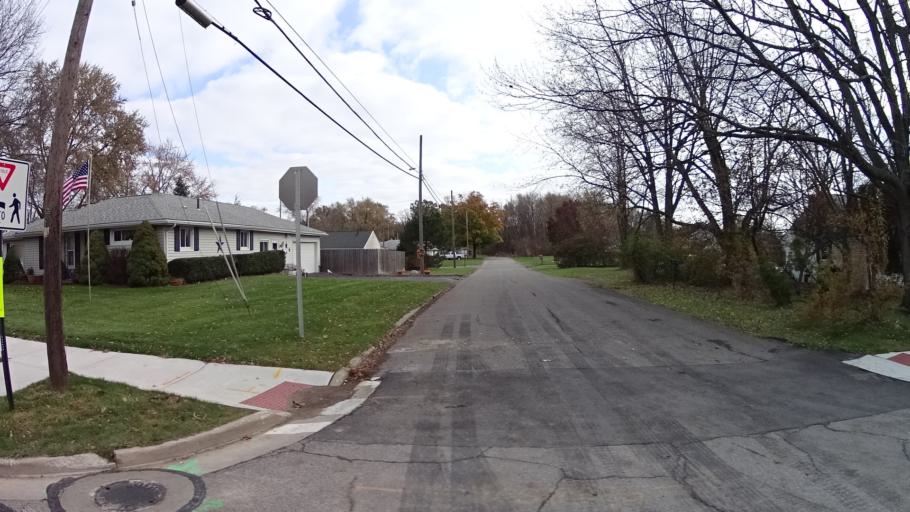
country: US
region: Ohio
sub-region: Lorain County
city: Sheffield Lake
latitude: 41.4826
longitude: -82.1132
